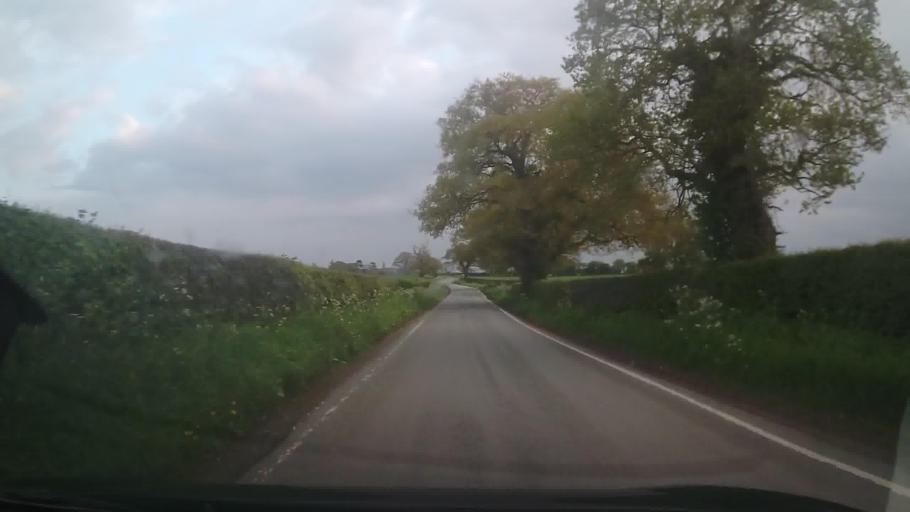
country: GB
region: England
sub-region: Shropshire
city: Ellesmere
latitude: 52.9253
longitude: -2.8009
